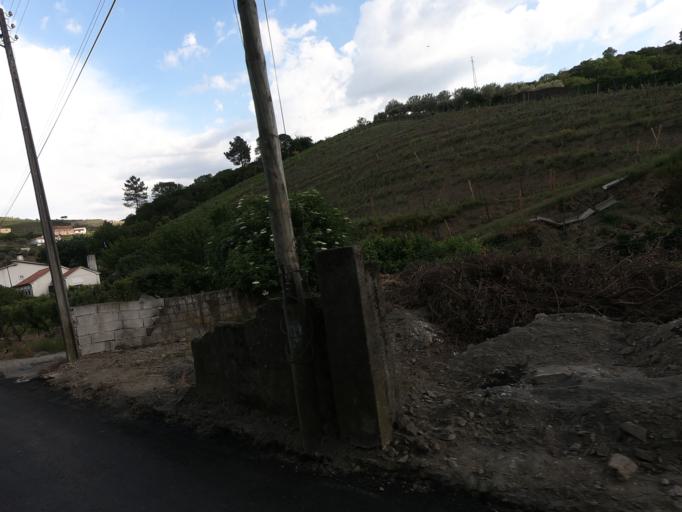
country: PT
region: Vila Real
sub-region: Santa Marta de Penaguiao
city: Santa Marta de Penaguiao
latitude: 41.2210
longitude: -7.7217
